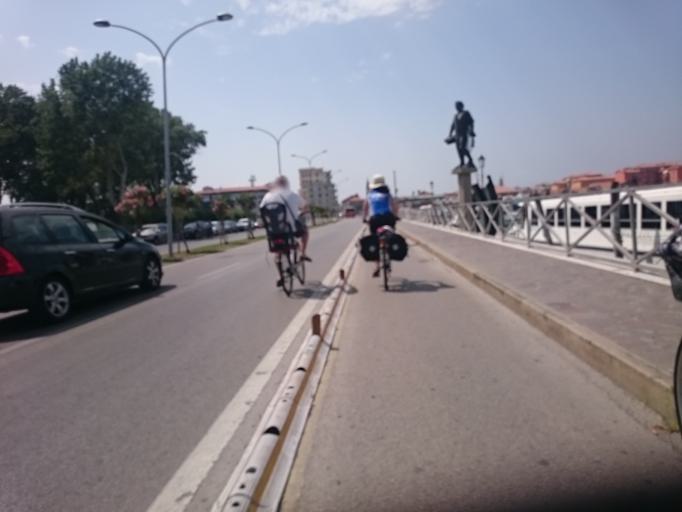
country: IT
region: Veneto
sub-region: Provincia di Venezia
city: Chioggia
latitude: 45.2169
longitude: 12.2861
